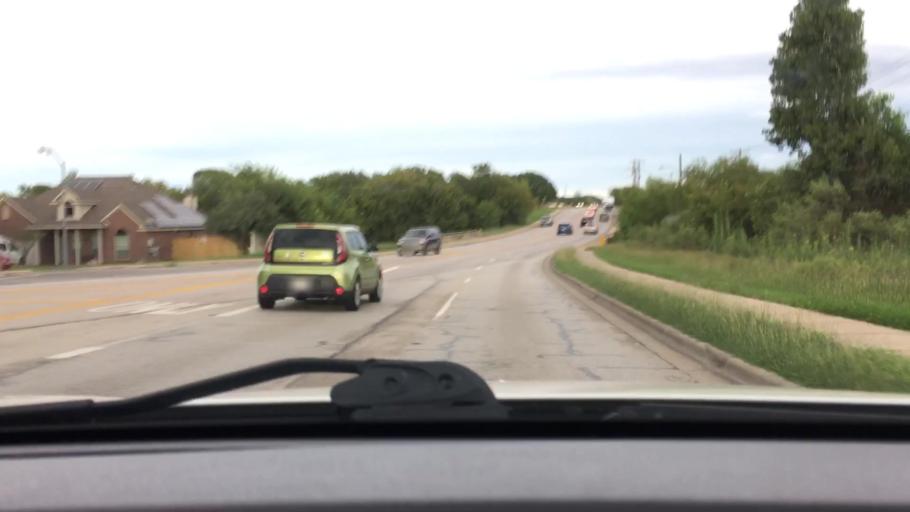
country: US
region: Texas
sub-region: Williamson County
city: Round Rock
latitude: 30.4962
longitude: -97.6524
